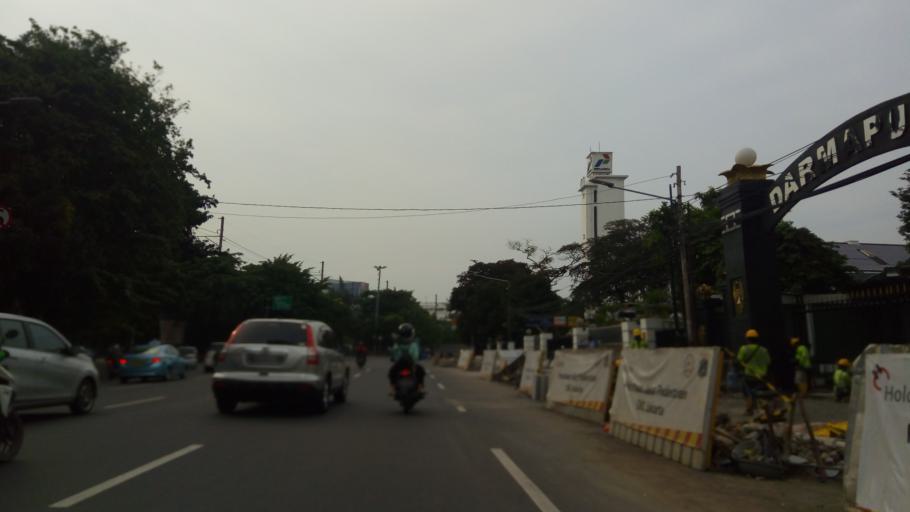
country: ID
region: Jakarta Raya
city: Jakarta
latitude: -6.1741
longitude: 106.8304
